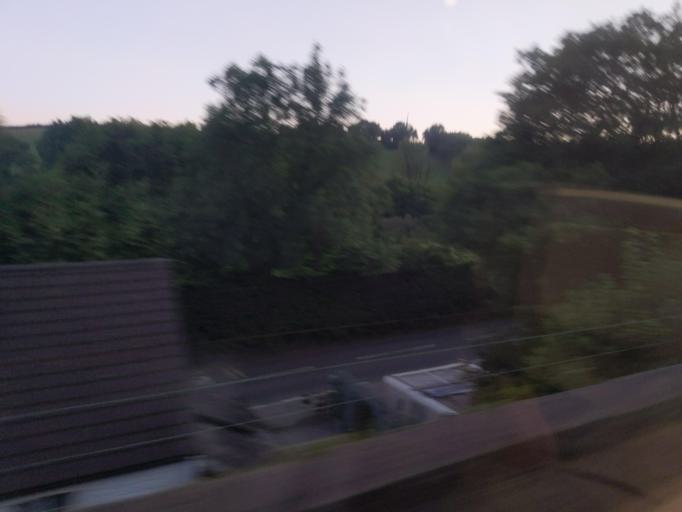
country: GB
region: England
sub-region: Devon
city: Buckfastleigh
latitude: 50.4316
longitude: -3.7830
